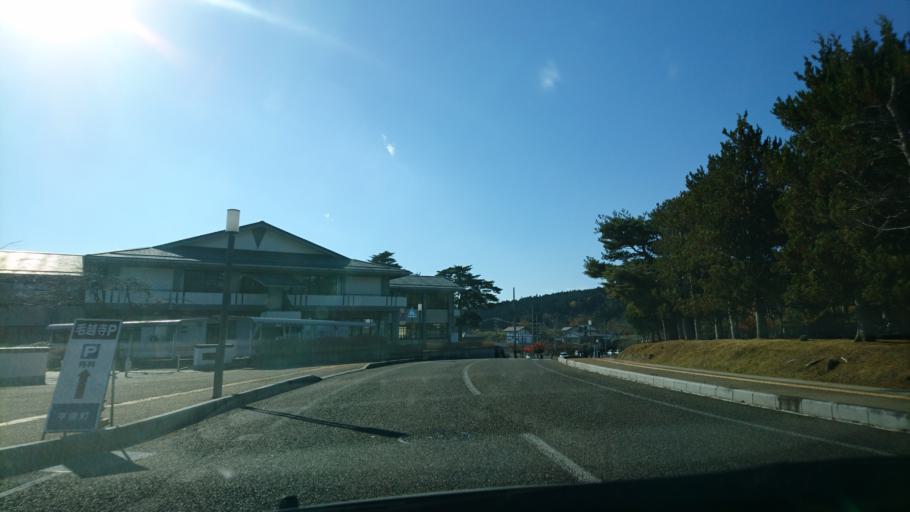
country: JP
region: Iwate
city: Ichinoseki
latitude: 38.9869
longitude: 141.1093
